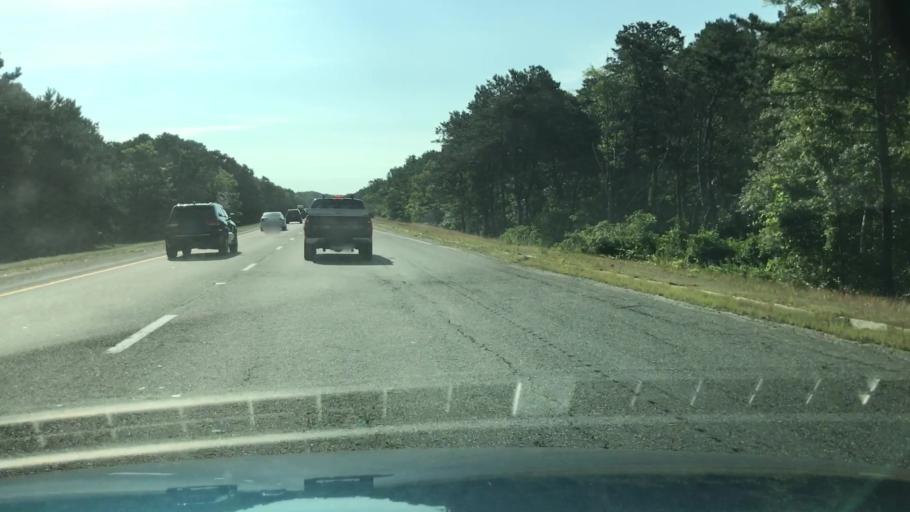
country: US
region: Massachusetts
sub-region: Barnstable County
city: Yarmouth Port
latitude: 41.6864
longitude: -70.2508
